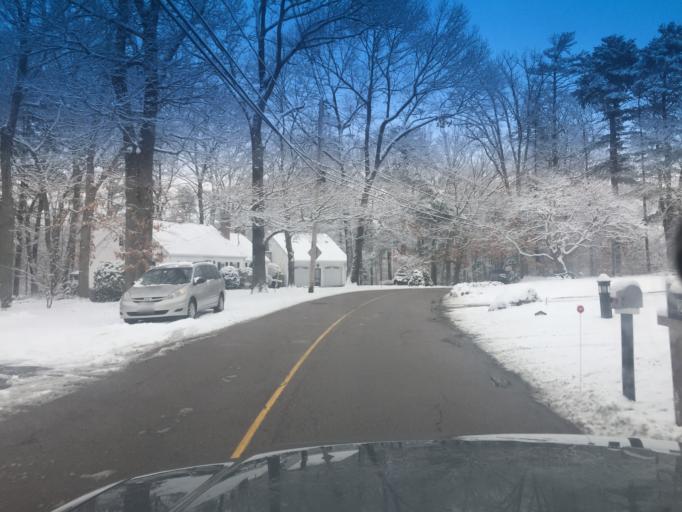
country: US
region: Massachusetts
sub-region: Norfolk County
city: Medway
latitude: 42.1235
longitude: -71.4175
